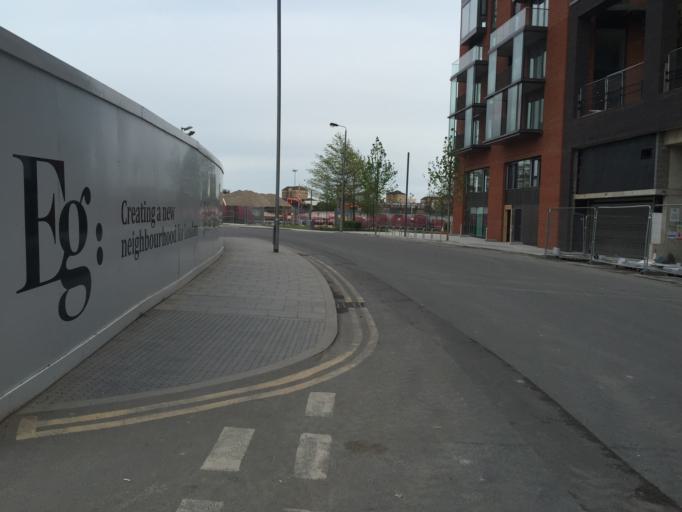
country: GB
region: England
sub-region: Greater London
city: Battersea
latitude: 51.4822
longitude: -0.1341
